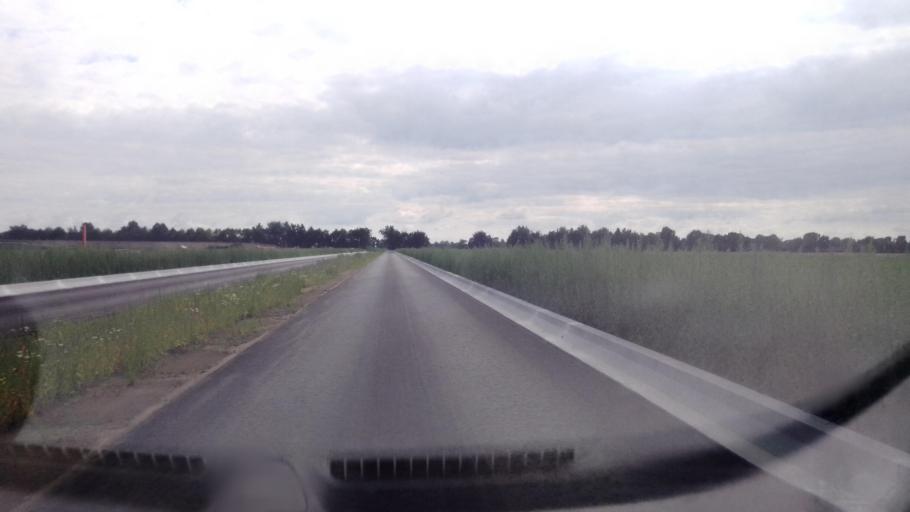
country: NL
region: Limburg
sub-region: Gemeente Peel en Maas
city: Maasbree
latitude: 51.4078
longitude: 6.0655
